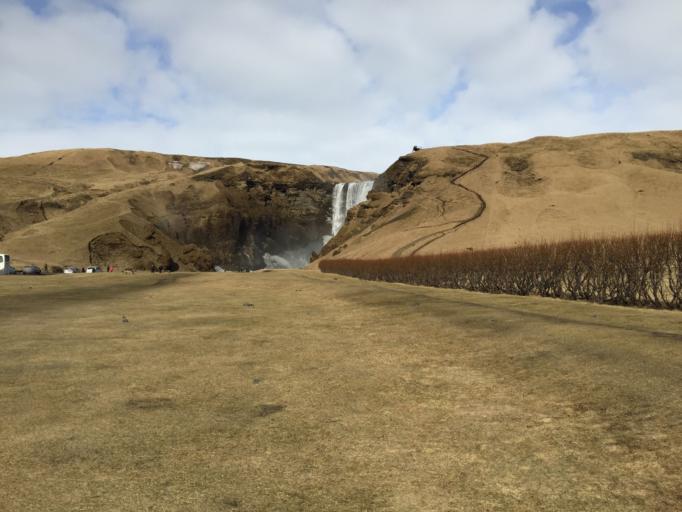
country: IS
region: South
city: Vestmannaeyjar
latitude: 63.5286
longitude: -19.5120
